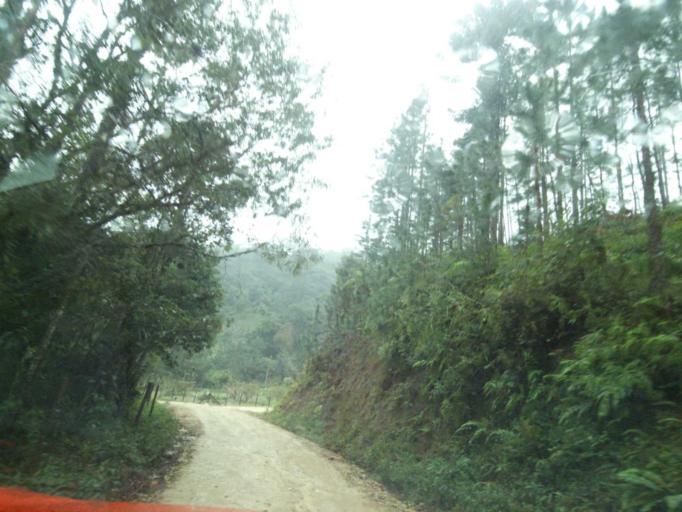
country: BR
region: Santa Catarina
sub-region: Anitapolis
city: Anitapolis
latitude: -27.9224
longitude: -49.1847
